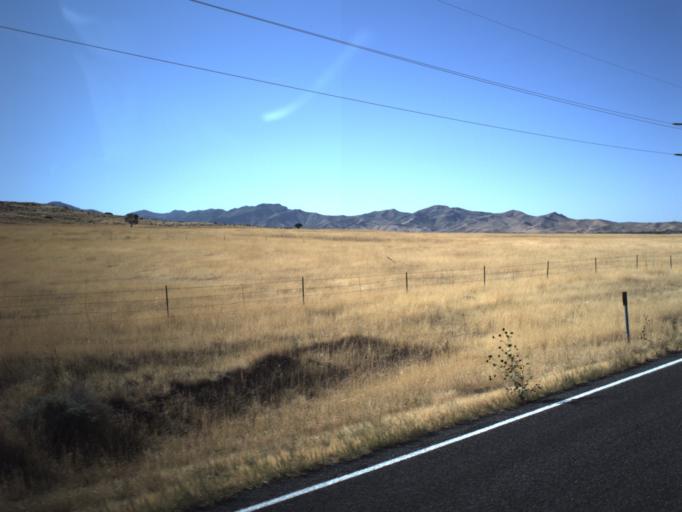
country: US
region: Utah
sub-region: Millard County
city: Delta
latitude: 39.4376
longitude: -112.3185
